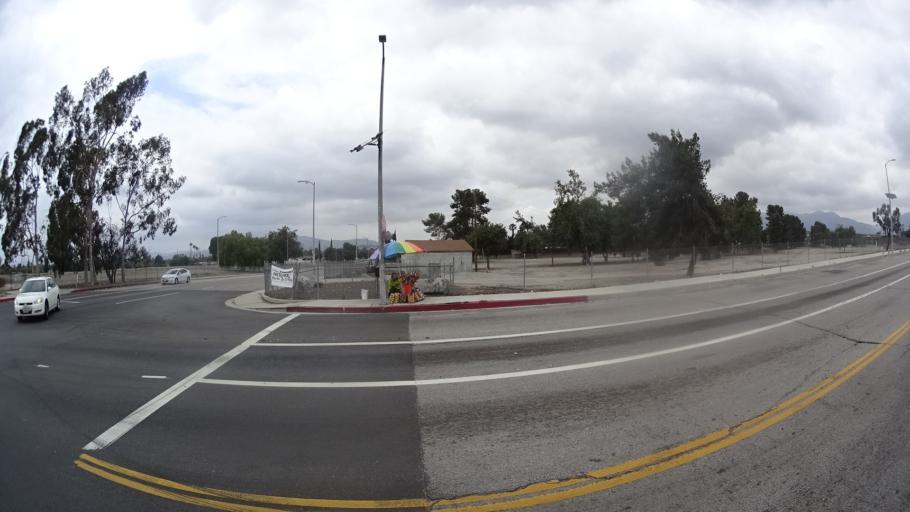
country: US
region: California
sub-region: Los Angeles County
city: San Fernando
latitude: 34.2601
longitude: -118.4449
